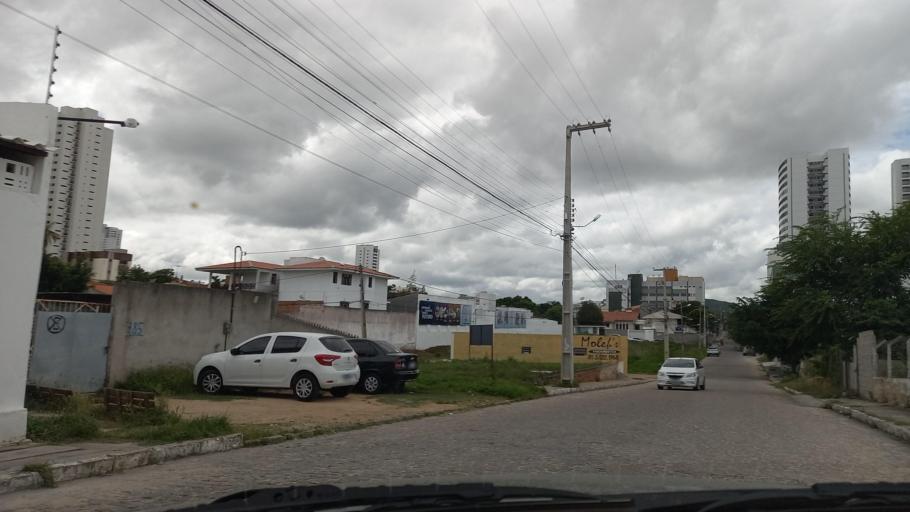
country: BR
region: Pernambuco
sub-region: Caruaru
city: Caruaru
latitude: -8.2725
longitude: -35.9686
